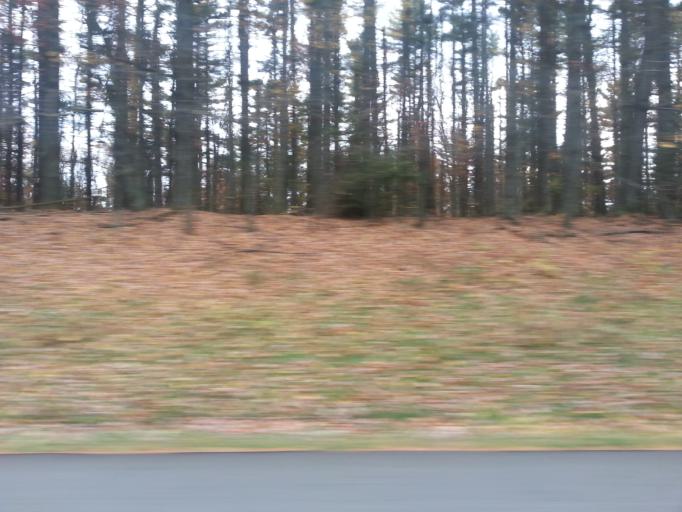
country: US
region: North Carolina
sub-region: Ashe County
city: Jefferson
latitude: 36.3600
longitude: -81.3697
